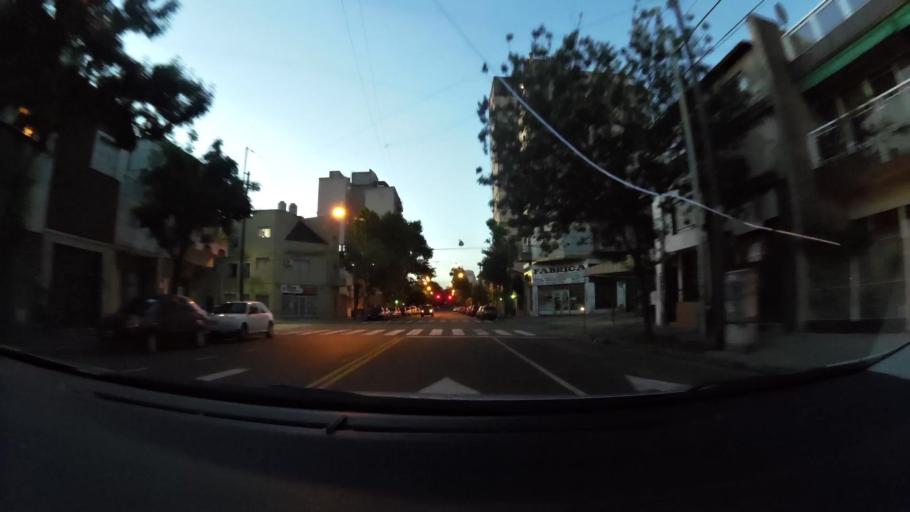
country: AR
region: Buenos Aires F.D.
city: Villa Santa Rita
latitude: -34.6377
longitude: -58.4605
